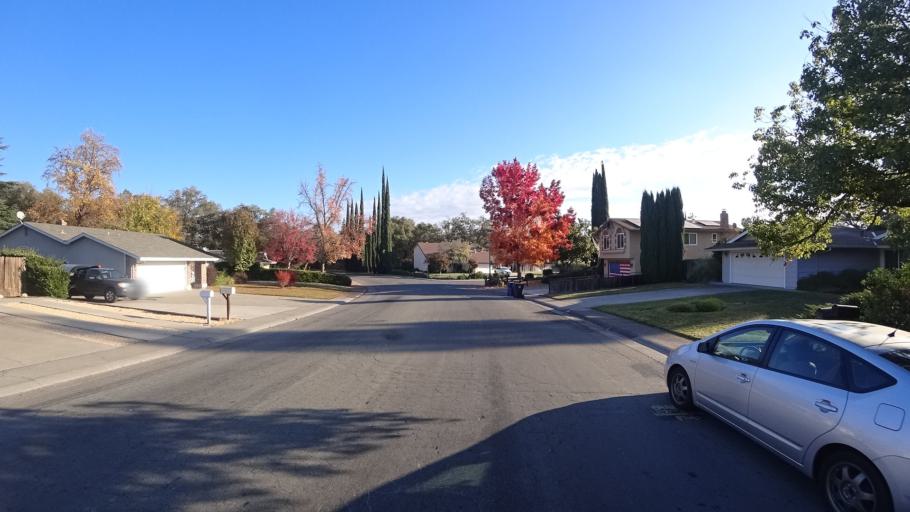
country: US
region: California
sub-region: Sacramento County
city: Citrus Heights
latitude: 38.7171
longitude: -121.2581
